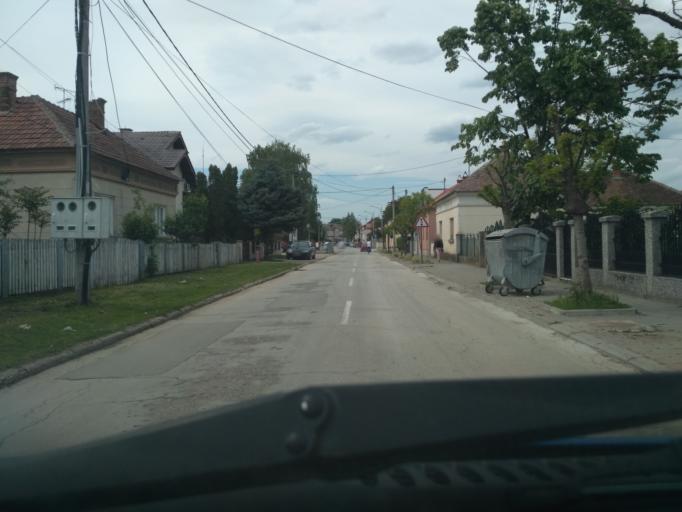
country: RS
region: Central Serbia
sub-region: Pomoravski Okrug
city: Svilajnac
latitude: 44.2285
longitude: 21.2015
